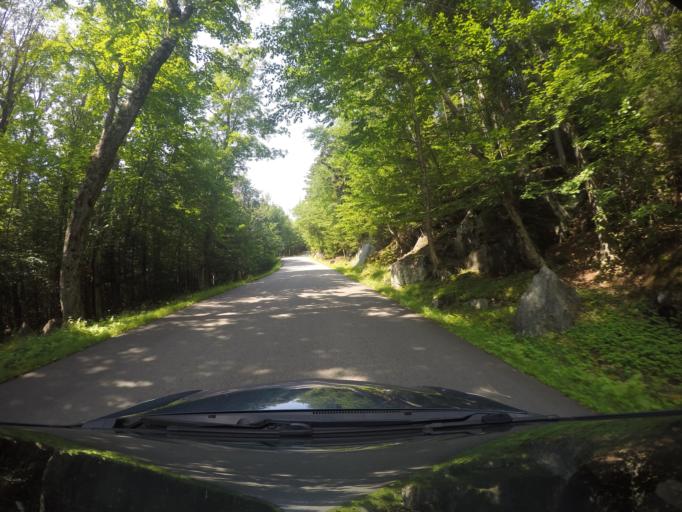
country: US
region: New Hampshire
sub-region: Coos County
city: Gorham
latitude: 44.2818
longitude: -71.2394
